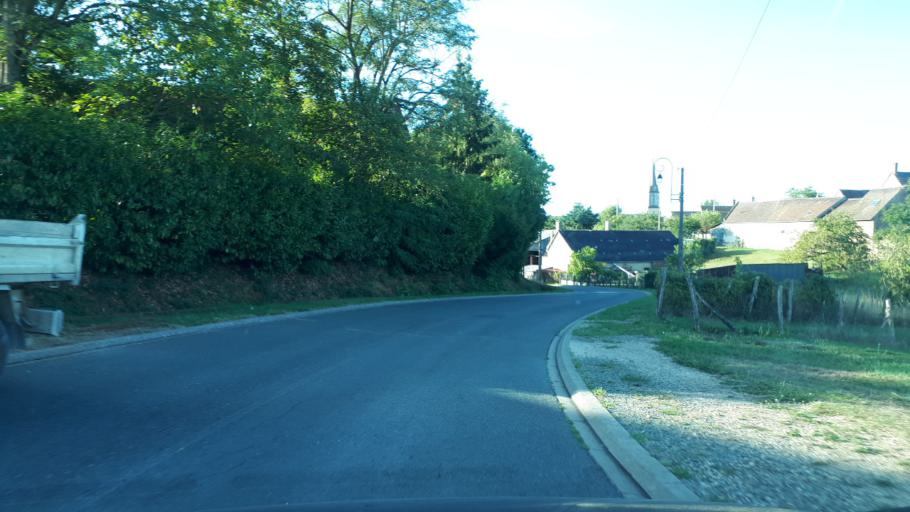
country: FR
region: Centre
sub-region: Departement du Loir-et-Cher
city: Lunay
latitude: 47.7553
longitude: 0.9383
